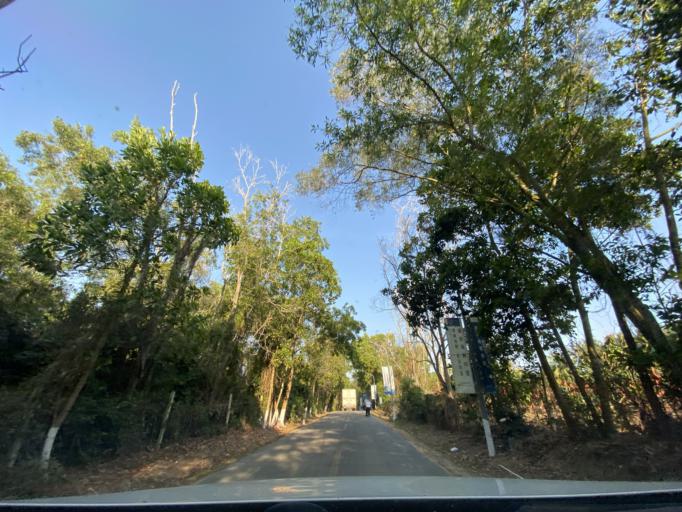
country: CN
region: Hainan
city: Yingzhou
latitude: 18.3878
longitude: 109.8250
